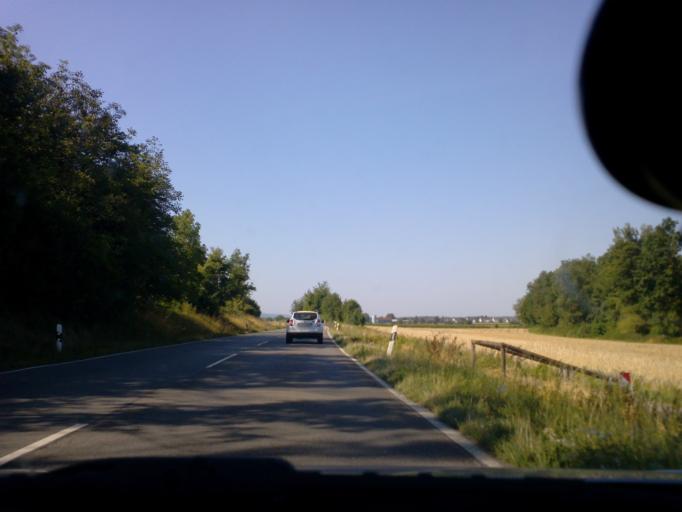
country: DE
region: Baden-Wuerttemberg
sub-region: Karlsruhe Region
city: Weingarten
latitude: 49.0698
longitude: 8.5411
